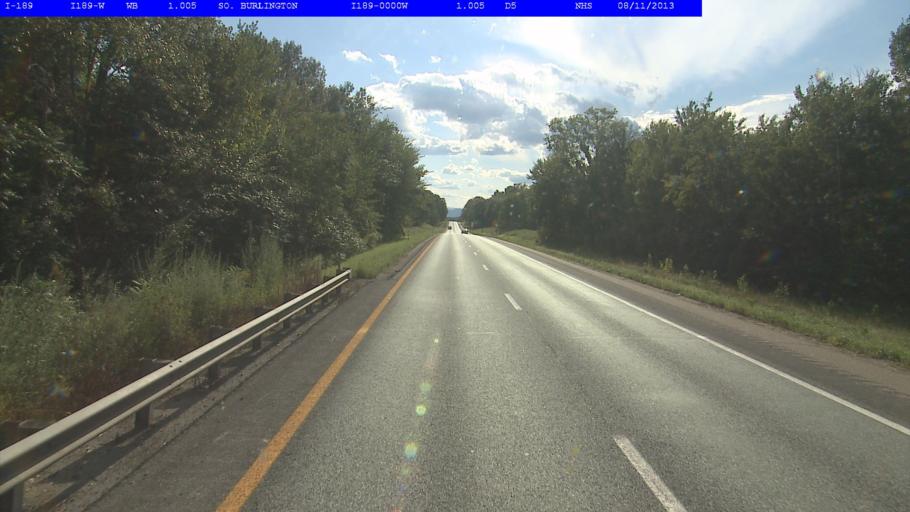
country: US
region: Vermont
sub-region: Chittenden County
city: South Burlington
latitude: 44.4515
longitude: -73.1902
